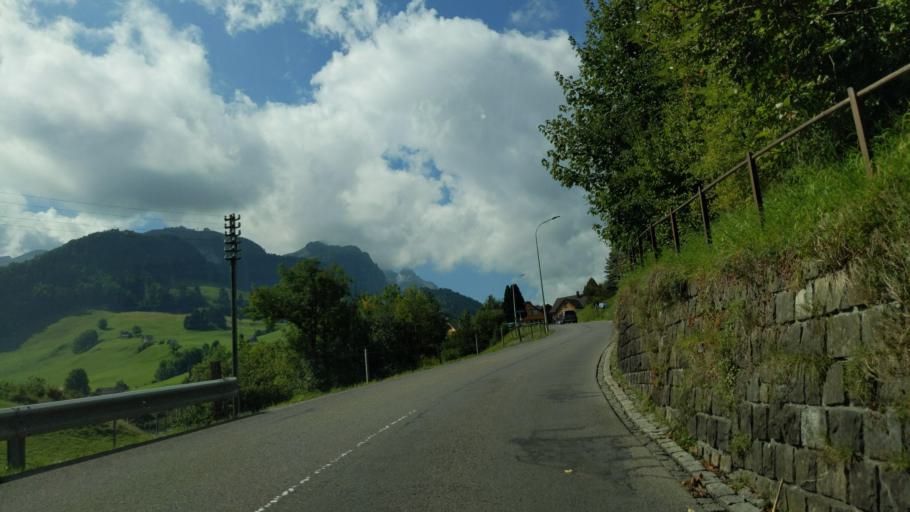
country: CH
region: Appenzell Innerrhoden
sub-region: Appenzell Inner Rhodes
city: Appenzell
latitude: 47.3077
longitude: 9.4352
